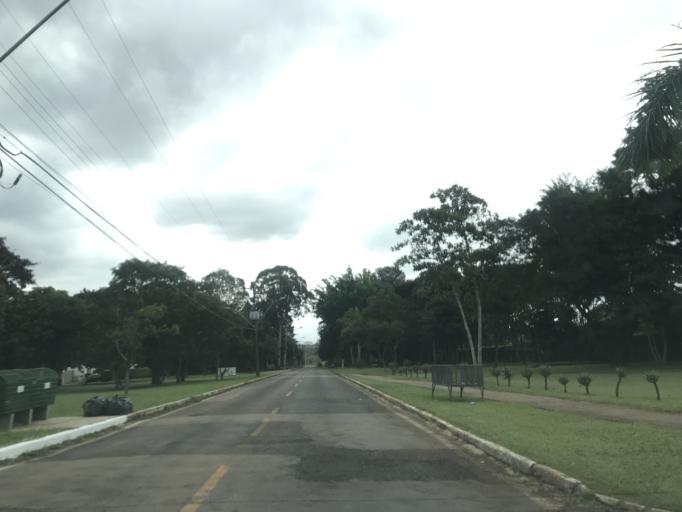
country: BR
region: Federal District
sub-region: Brasilia
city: Brasilia
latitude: -15.8960
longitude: -47.9317
